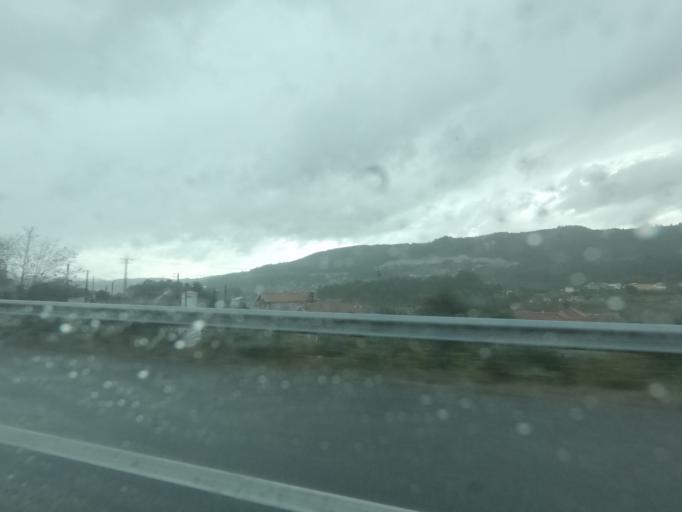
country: ES
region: Galicia
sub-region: Provincia de Pontevedra
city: Pontevedra
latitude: 42.3801
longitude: -8.6368
